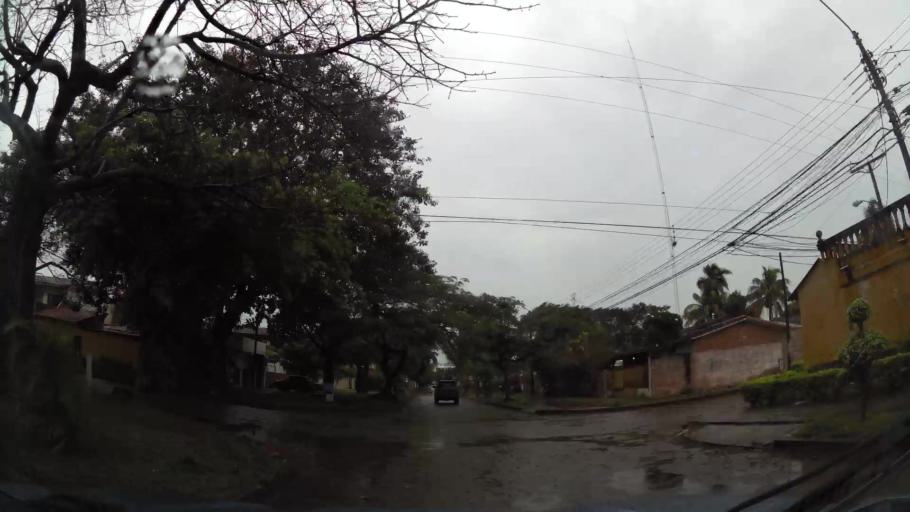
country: BO
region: Santa Cruz
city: Santa Cruz de la Sierra
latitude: -17.7881
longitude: -63.2092
